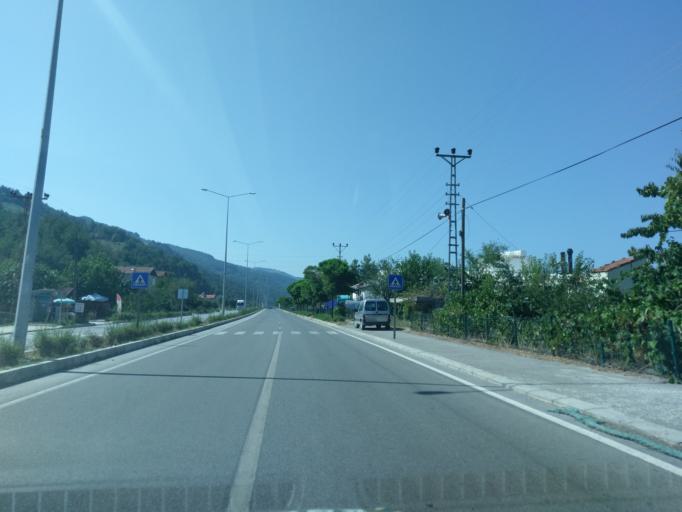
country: TR
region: Samsun
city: Yakakent
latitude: 41.6423
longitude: 35.4895
